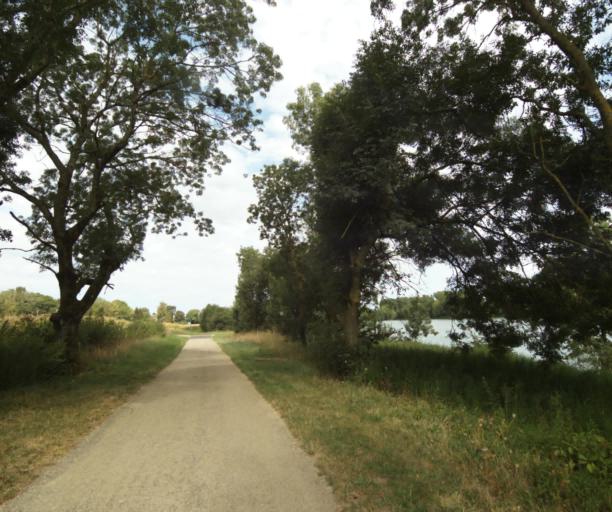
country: FR
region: Bourgogne
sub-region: Departement de Saone-et-Loire
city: Tournus
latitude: 46.5471
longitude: 4.9225
